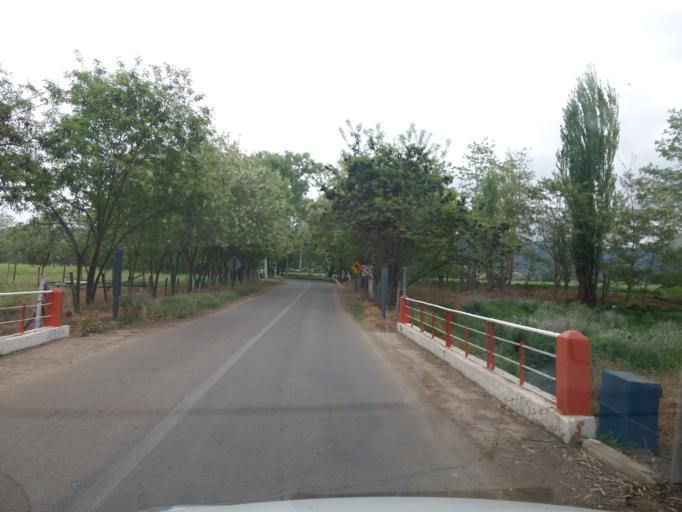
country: CL
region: Valparaiso
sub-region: Provincia de Quillota
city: Quillota
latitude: -32.8898
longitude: -71.3100
